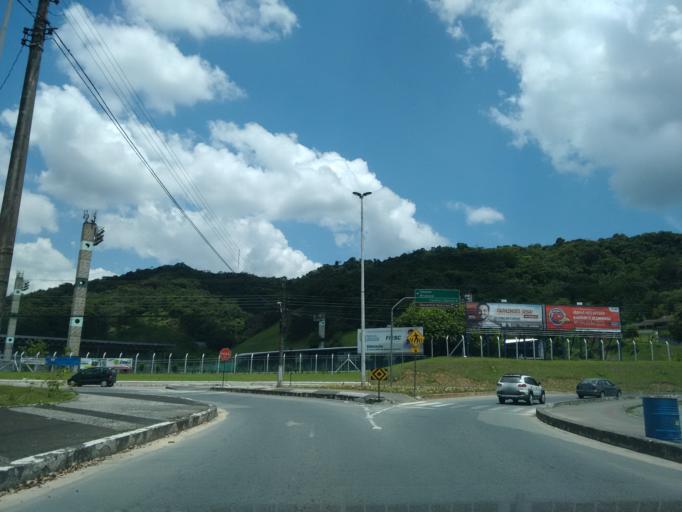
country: BR
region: Santa Catarina
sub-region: Blumenau
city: Blumenau
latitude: -26.9070
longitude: -49.0339
